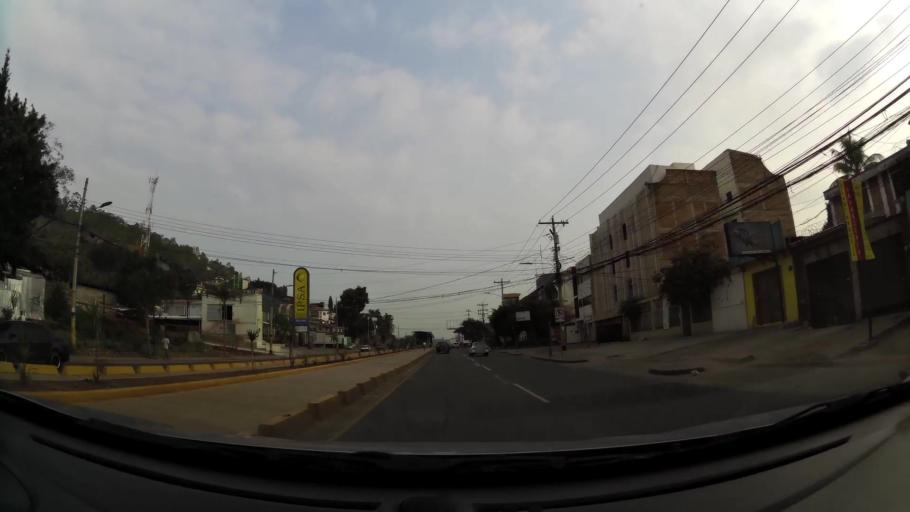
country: HN
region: Francisco Morazan
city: Tegucigalpa
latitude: 14.0920
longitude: -87.1975
